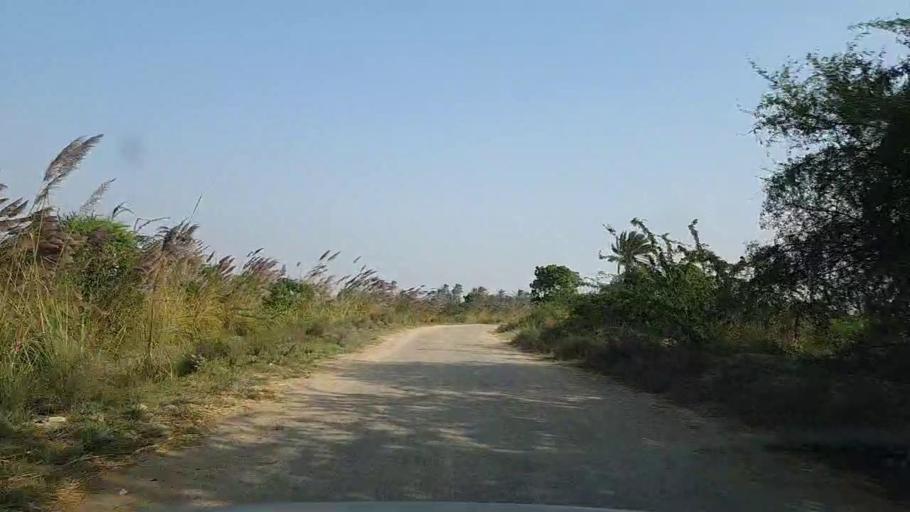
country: PK
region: Sindh
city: Mirpur Sakro
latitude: 24.5943
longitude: 67.6052
